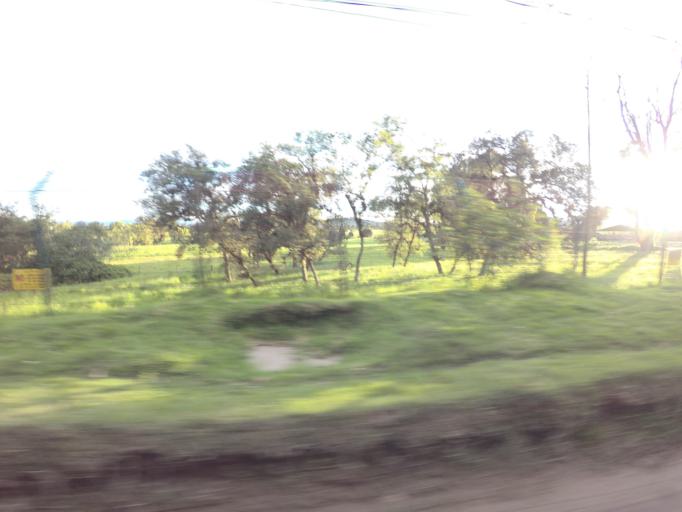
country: CO
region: Cundinamarca
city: Cota
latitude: 4.7933
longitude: -74.0300
